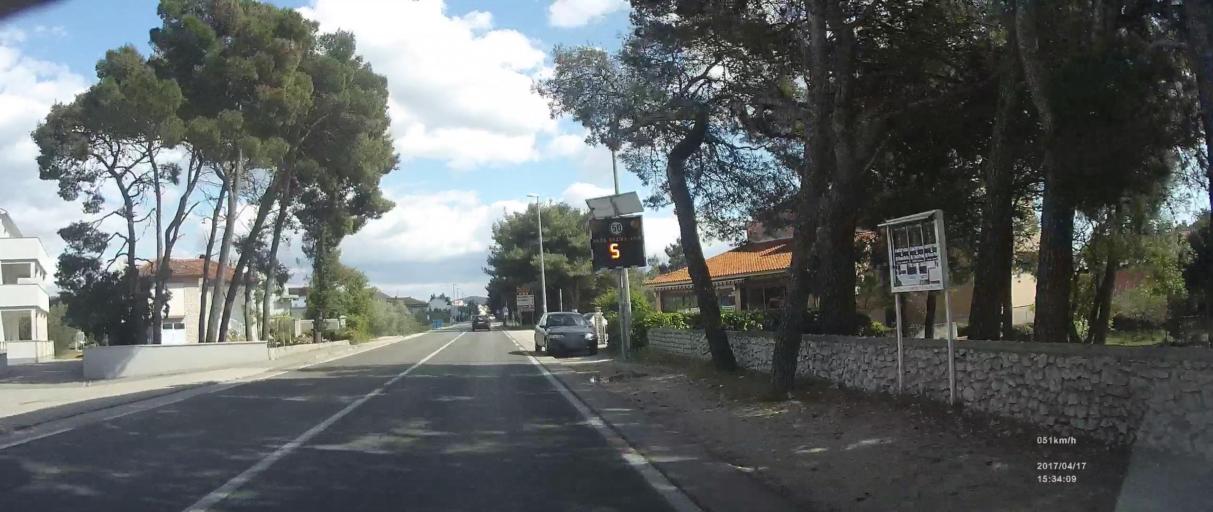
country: HR
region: Sibensko-Kniniska
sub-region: Grad Sibenik
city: Brodarica
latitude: 43.6815
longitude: 15.9159
